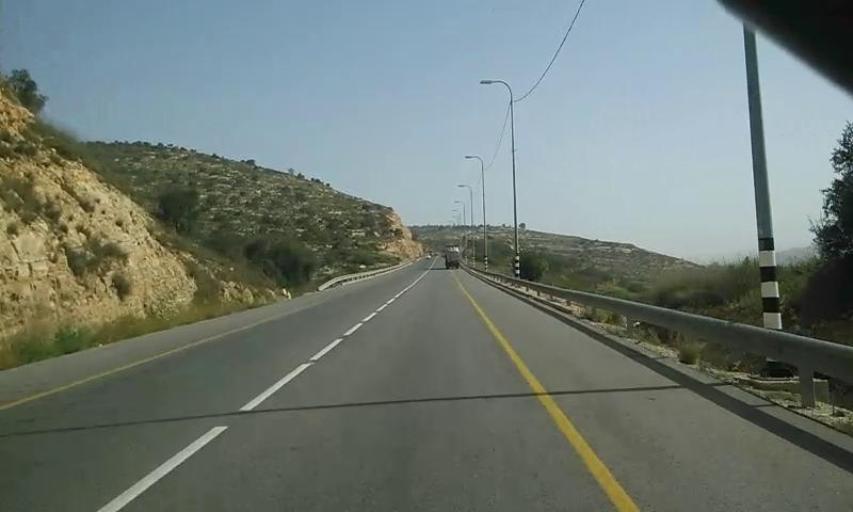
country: PS
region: West Bank
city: Yatma
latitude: 32.1077
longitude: 35.2563
